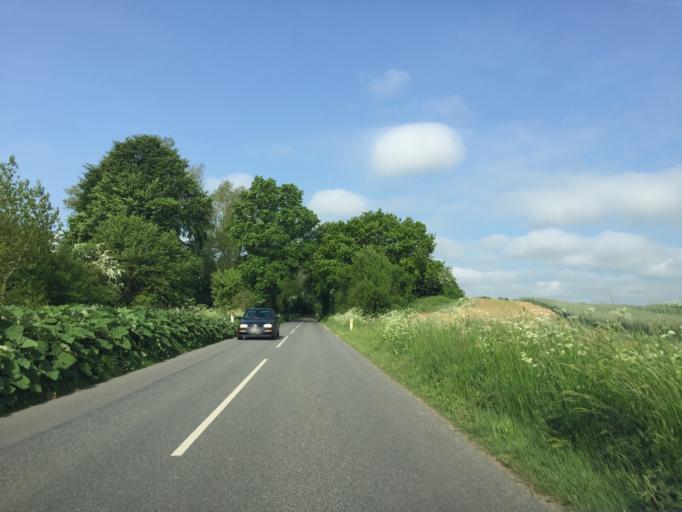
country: DK
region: South Denmark
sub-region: Svendborg Kommune
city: Thuro By
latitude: 55.1402
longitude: 10.7705
